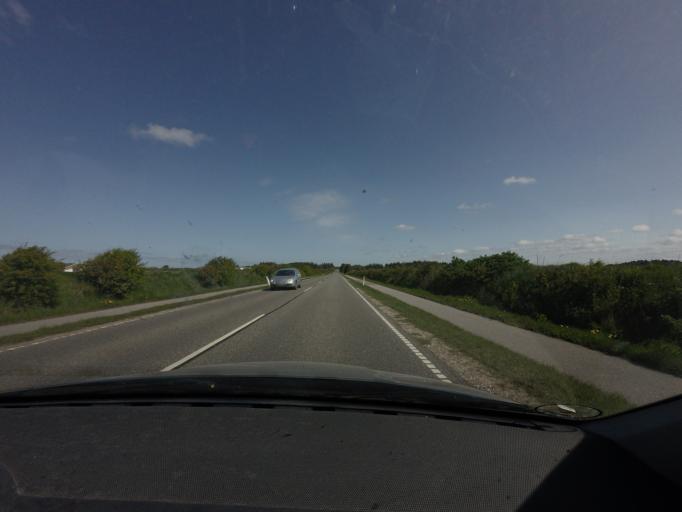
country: DK
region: North Denmark
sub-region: Jammerbugt Kommune
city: Pandrup
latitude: 57.2949
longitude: 9.6951
